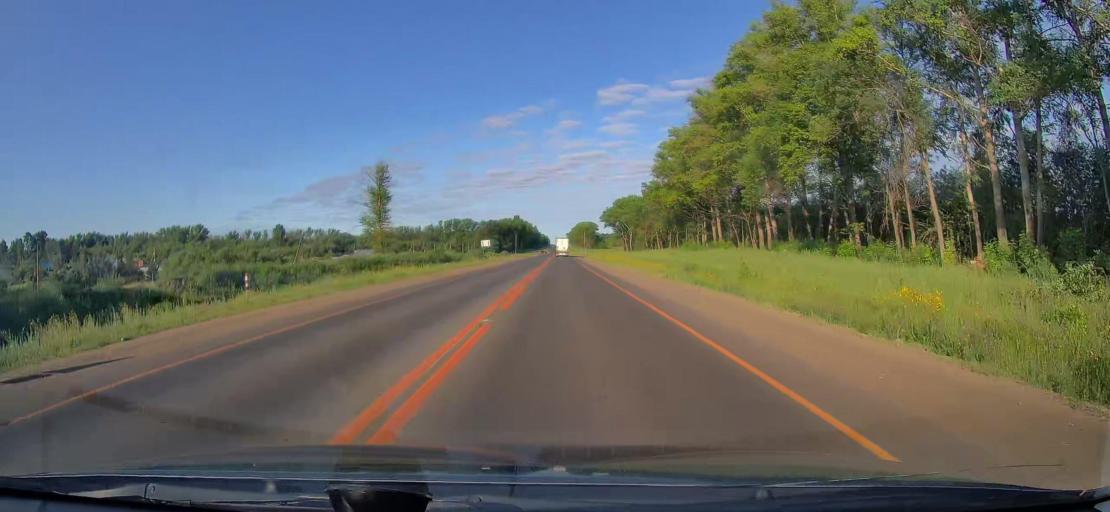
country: RU
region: Tula
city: Bol'shoye Skuratovo
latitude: 53.4418
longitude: 36.8289
